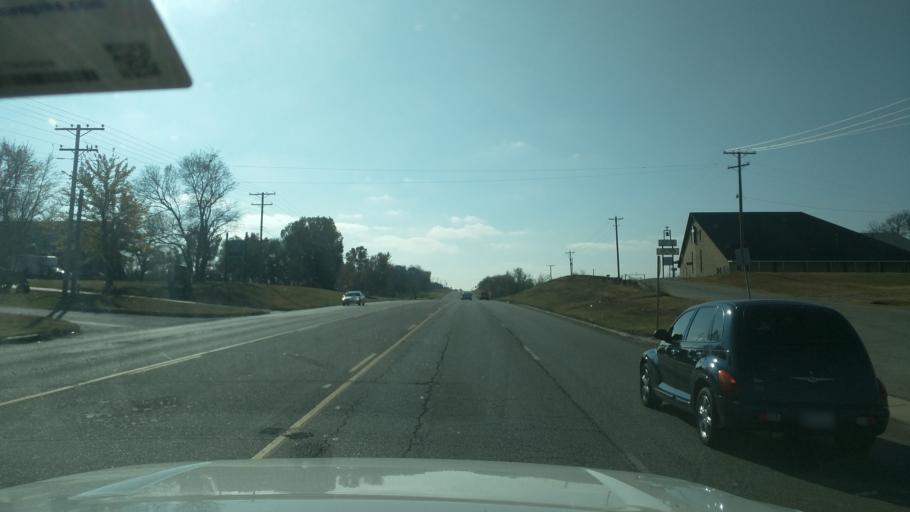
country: US
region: Oklahoma
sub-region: Washington County
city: Bartlesville
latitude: 36.6958
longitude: -95.9352
